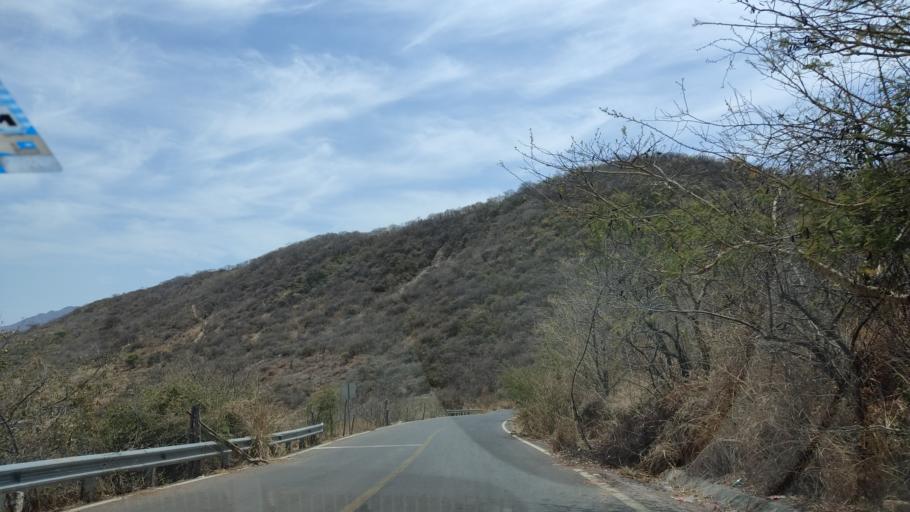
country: MX
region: Nayarit
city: Santa Maria del Oro
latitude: 21.5129
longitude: -104.5945
